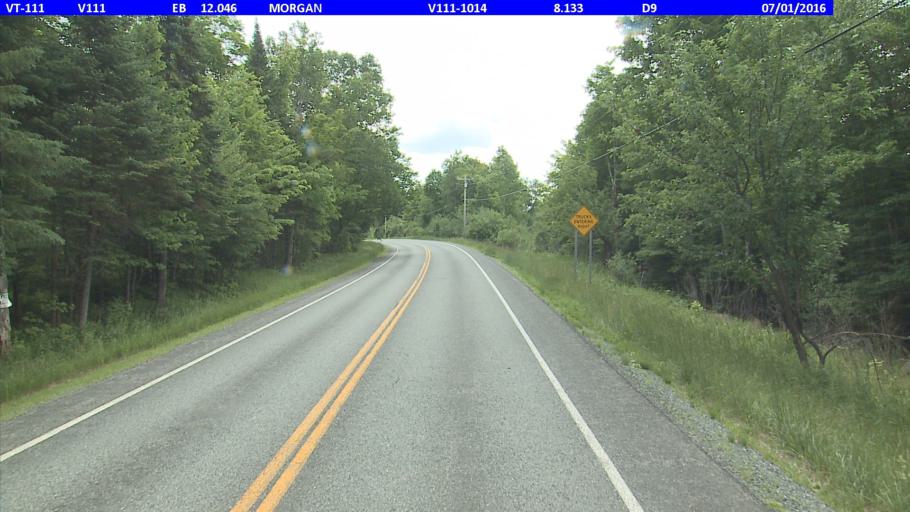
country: US
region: Vermont
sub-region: Orleans County
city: Newport
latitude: 44.8670
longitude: -71.9575
